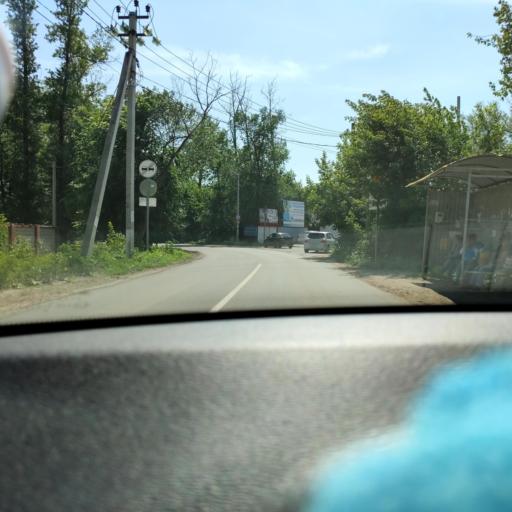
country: RU
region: Samara
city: Novokuybyshevsk
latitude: 53.1593
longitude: 49.9476
